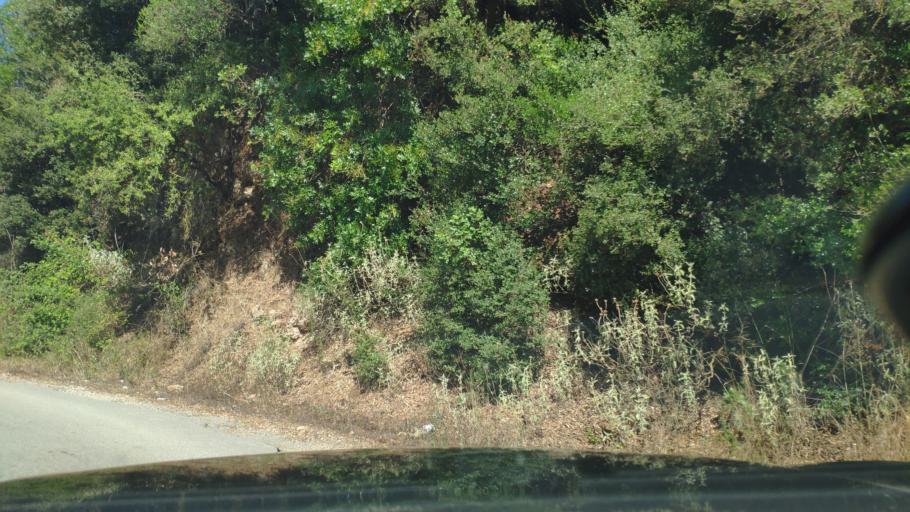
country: GR
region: West Greece
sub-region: Nomos Aitolias kai Akarnanias
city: Katouna
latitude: 38.8074
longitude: 21.1070
